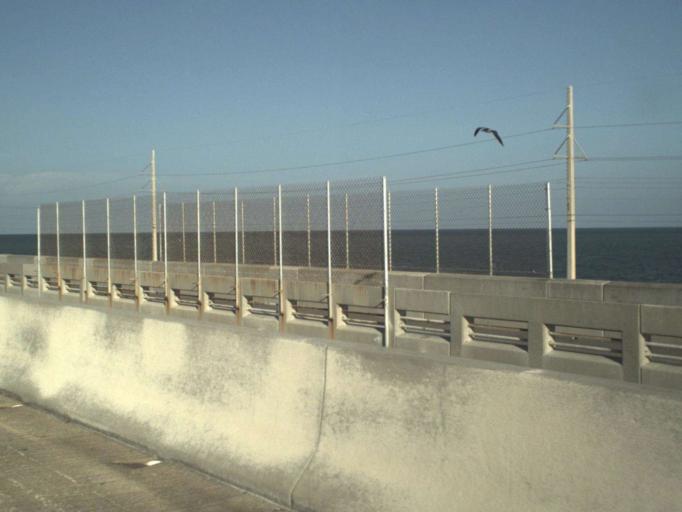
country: US
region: Florida
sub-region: Monroe County
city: Marathon
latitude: 24.7983
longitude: -80.8640
